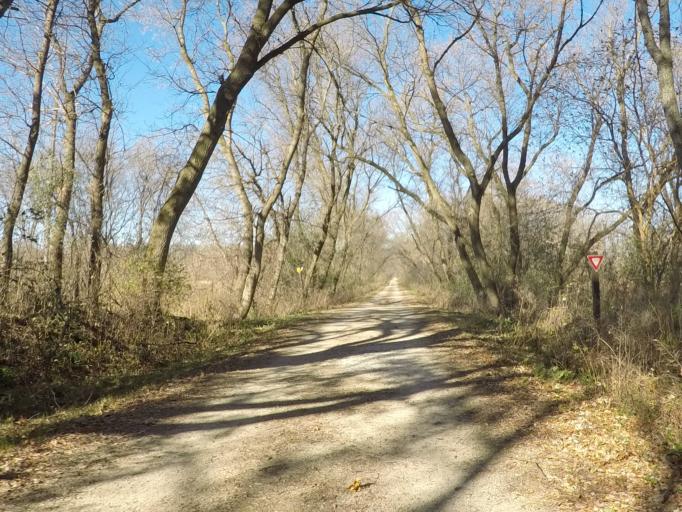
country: US
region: Wisconsin
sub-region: Dane County
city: Deerfield
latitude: 43.0487
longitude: -89.0596
